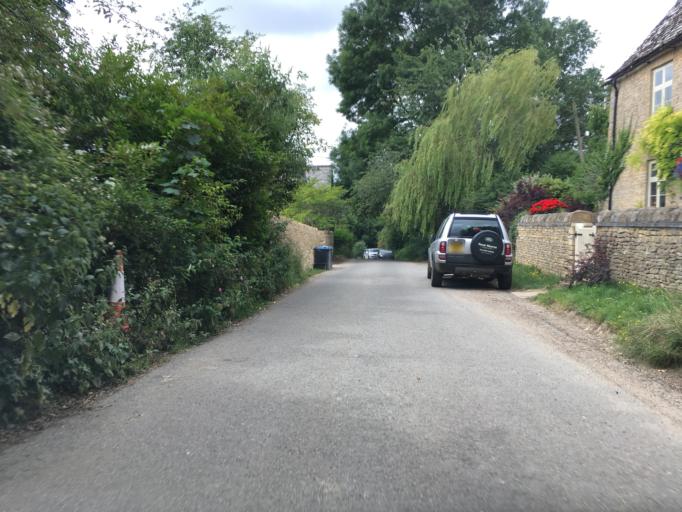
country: GB
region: England
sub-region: Oxfordshire
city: Charlbury
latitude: 51.8993
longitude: -1.5044
